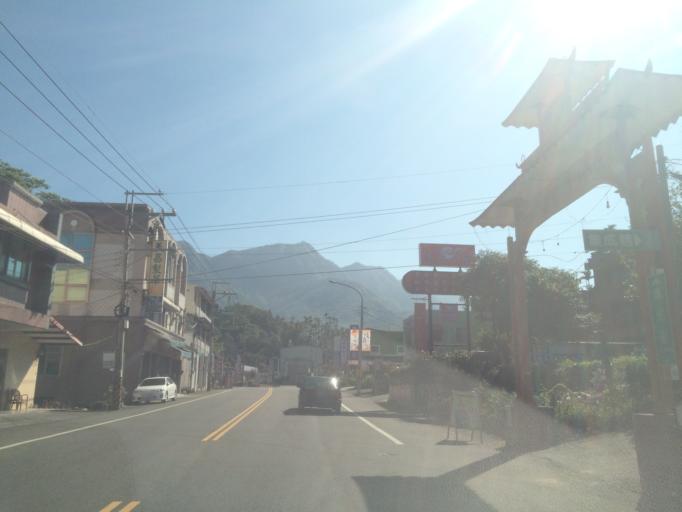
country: TW
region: Taiwan
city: Lugu
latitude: 23.7325
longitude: 120.7685
